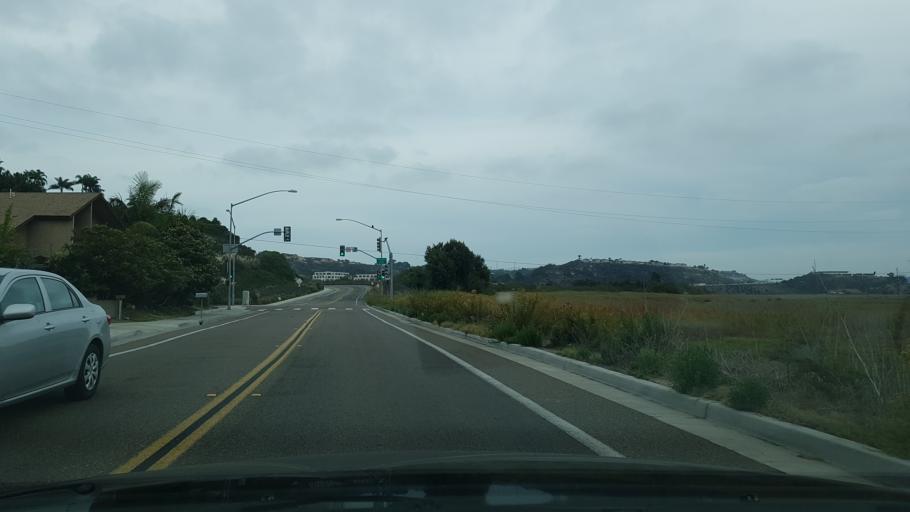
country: US
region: California
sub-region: San Diego County
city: Del Mar
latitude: 32.9311
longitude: -117.2482
